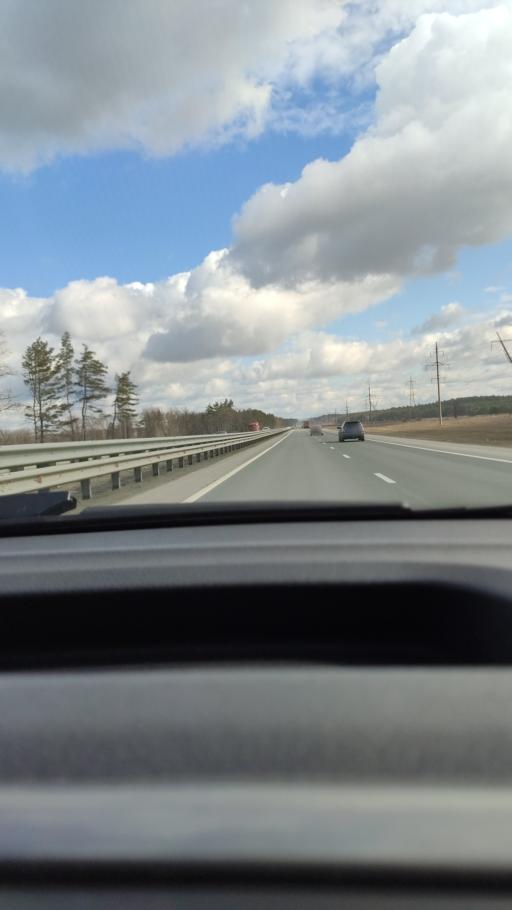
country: RU
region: Samara
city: Povolzhskiy
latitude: 53.5151
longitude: 49.6502
